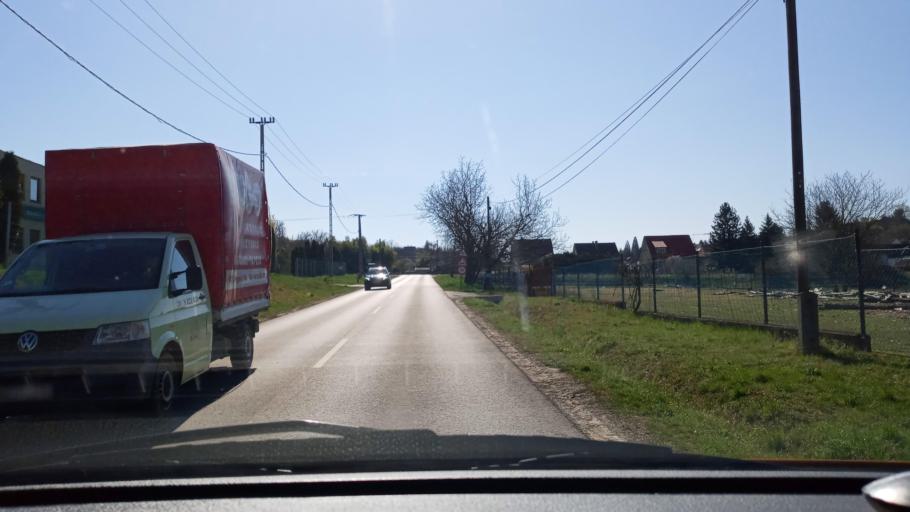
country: HU
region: Baranya
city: Pecs
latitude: 46.0877
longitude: 18.2855
